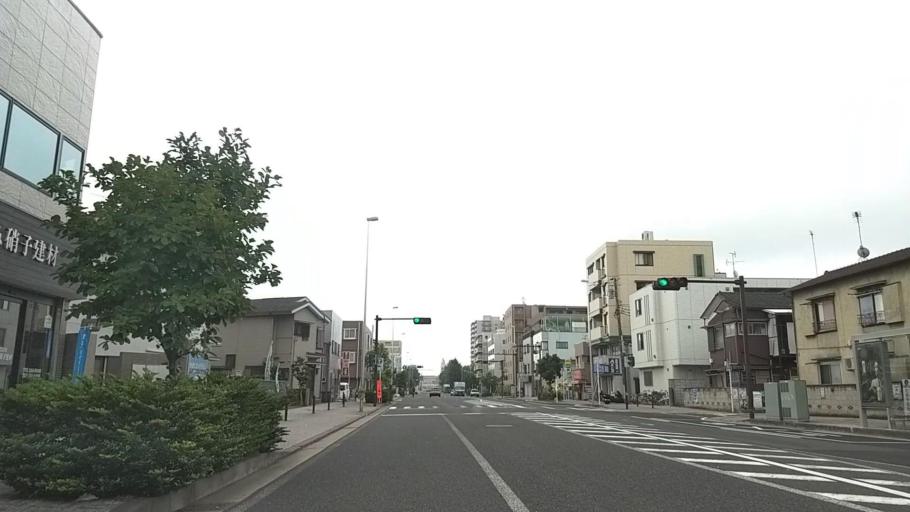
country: JP
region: Kanagawa
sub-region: Kawasaki-shi
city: Kawasaki
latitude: 35.5157
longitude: 139.6961
